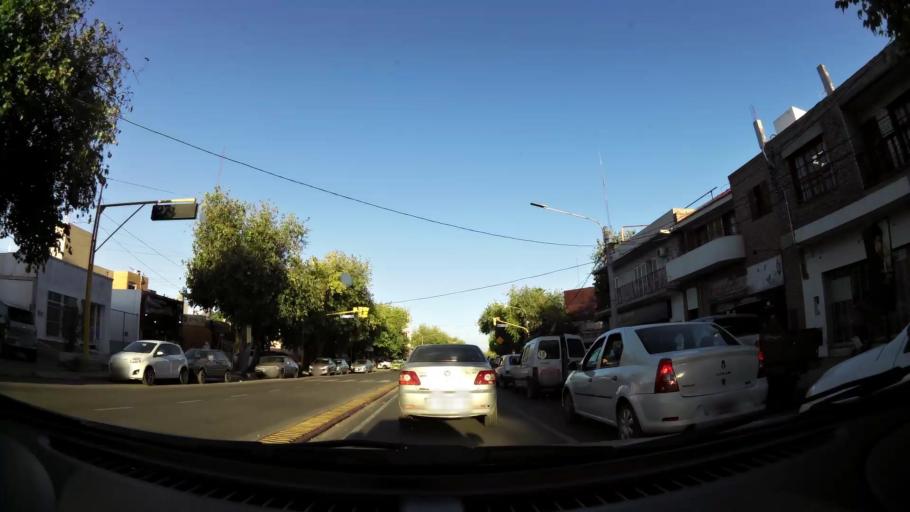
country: AR
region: San Juan
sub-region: Departamento de Santa Lucia
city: Santa Lucia
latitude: -31.5412
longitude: -68.4968
